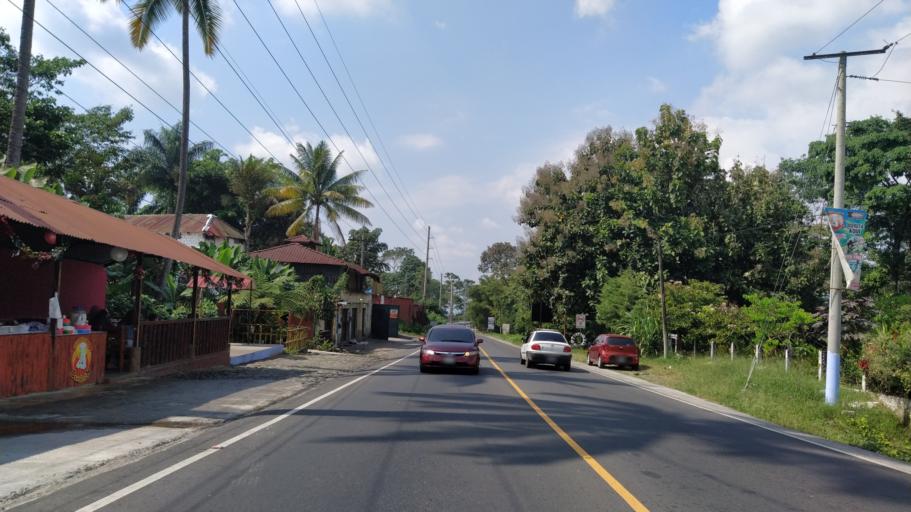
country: GT
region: Quetzaltenango
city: El Palmar
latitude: 14.6333
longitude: -91.5827
